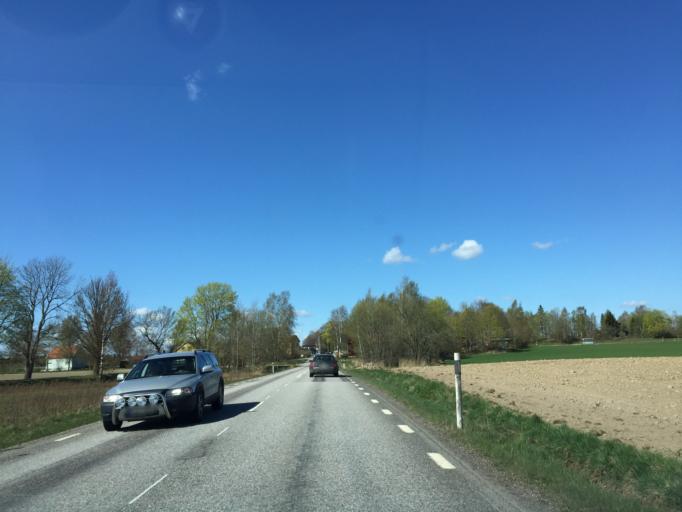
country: SE
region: OErebro
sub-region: Hallsbergs Kommun
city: Skollersta
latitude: 59.1271
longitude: 15.3255
